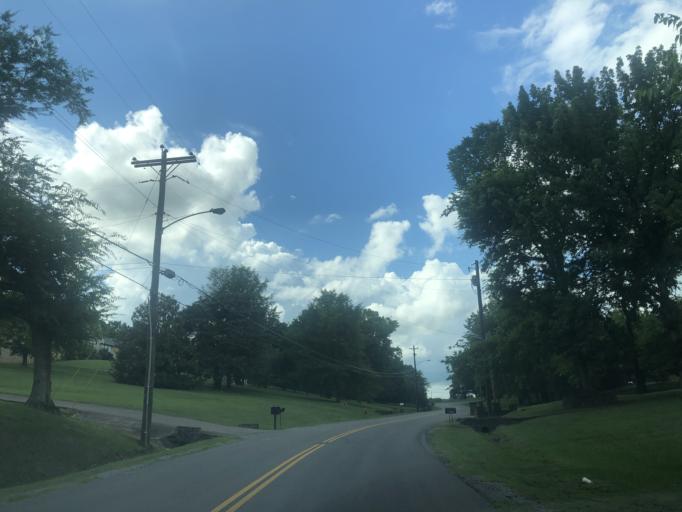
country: US
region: Tennessee
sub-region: Davidson County
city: Nashville
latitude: 36.2136
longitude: -86.8553
